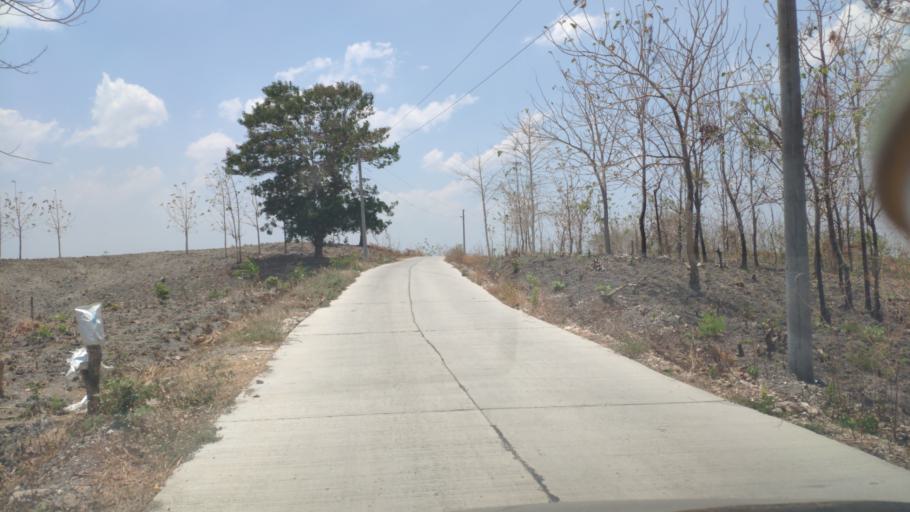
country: ID
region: Central Java
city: Temulus
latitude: -7.2884
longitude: 111.3778
